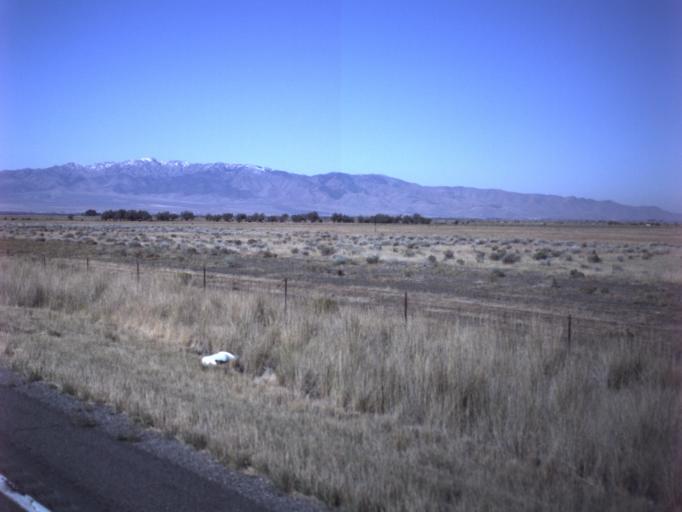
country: US
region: Utah
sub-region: Tooele County
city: Erda
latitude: 40.6321
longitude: -112.3364
